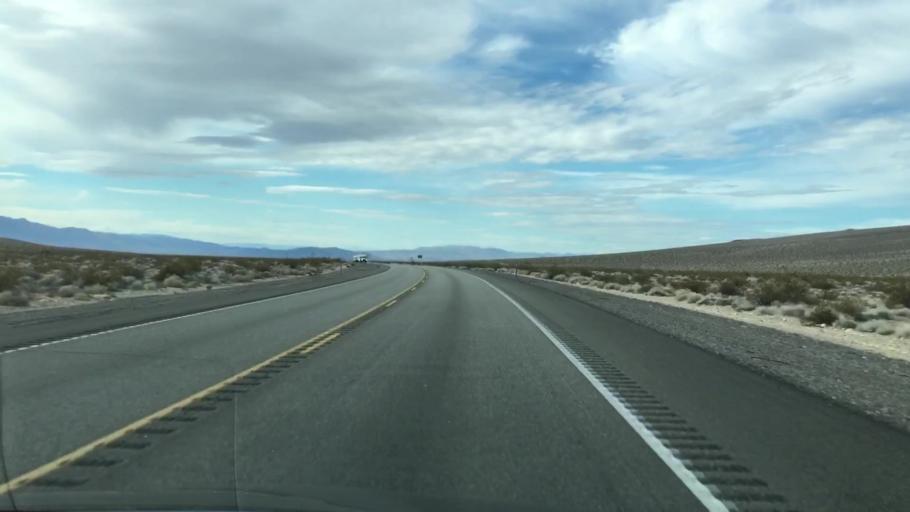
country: US
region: Nevada
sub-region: Nye County
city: Beatty
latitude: 36.6315
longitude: -116.3213
